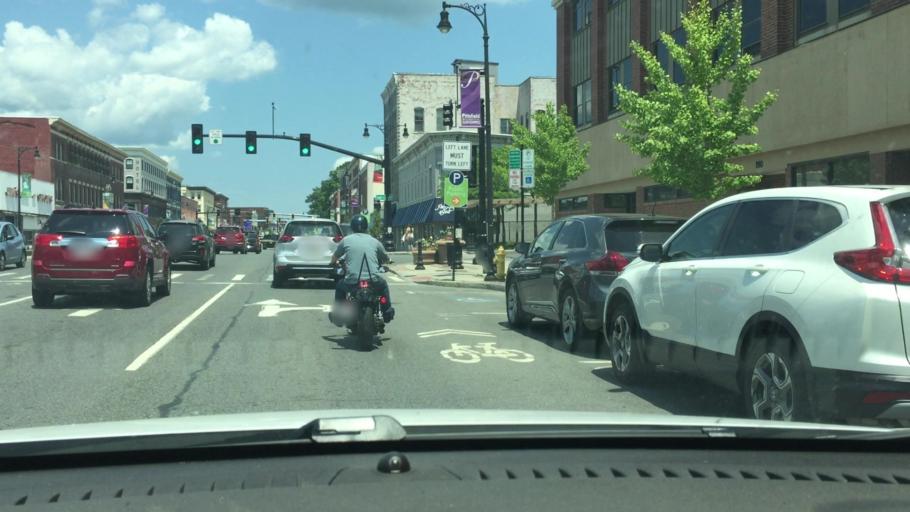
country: US
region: Massachusetts
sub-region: Berkshire County
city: Pittsfield
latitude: 42.4512
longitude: -73.2531
